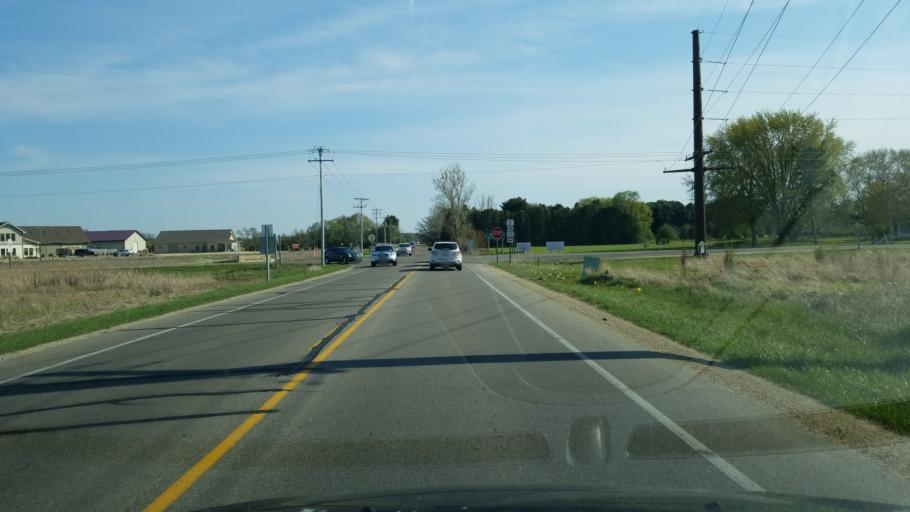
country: US
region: Wisconsin
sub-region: Dane County
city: Fitchburg
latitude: 42.9298
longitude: -89.4382
